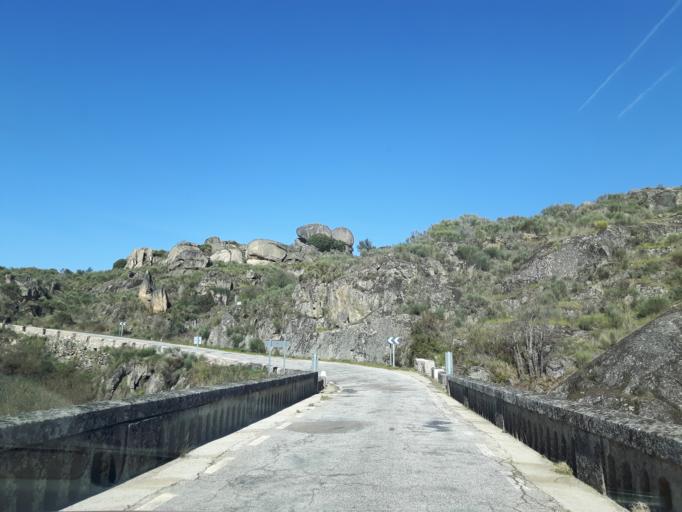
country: ES
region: Castille and Leon
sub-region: Provincia de Salamanca
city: Saldeana
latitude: 40.9953
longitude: -6.6266
